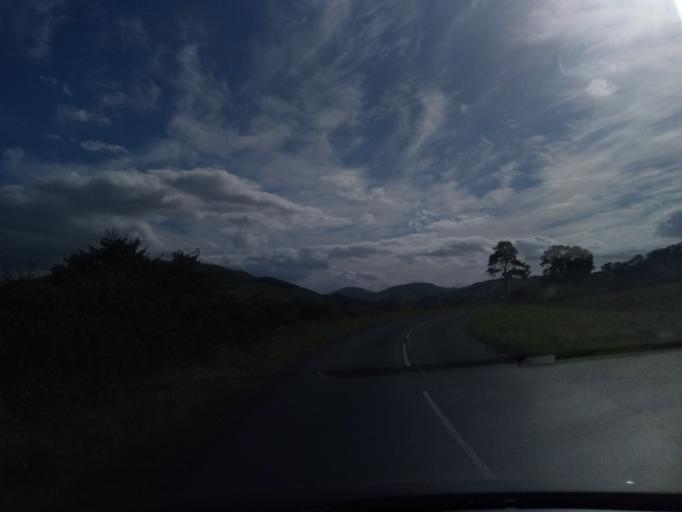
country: GB
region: Scotland
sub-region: The Scottish Borders
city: Coldstream
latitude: 55.5586
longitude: -2.2679
